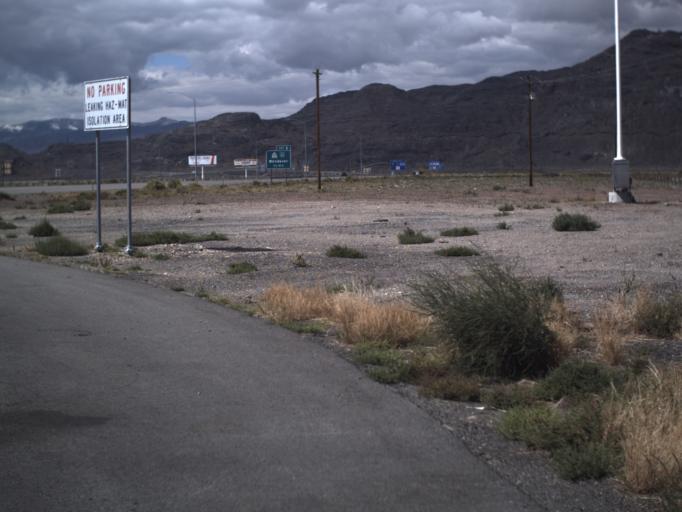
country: US
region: Utah
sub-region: Tooele County
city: Wendover
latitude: 40.7459
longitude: -113.9907
